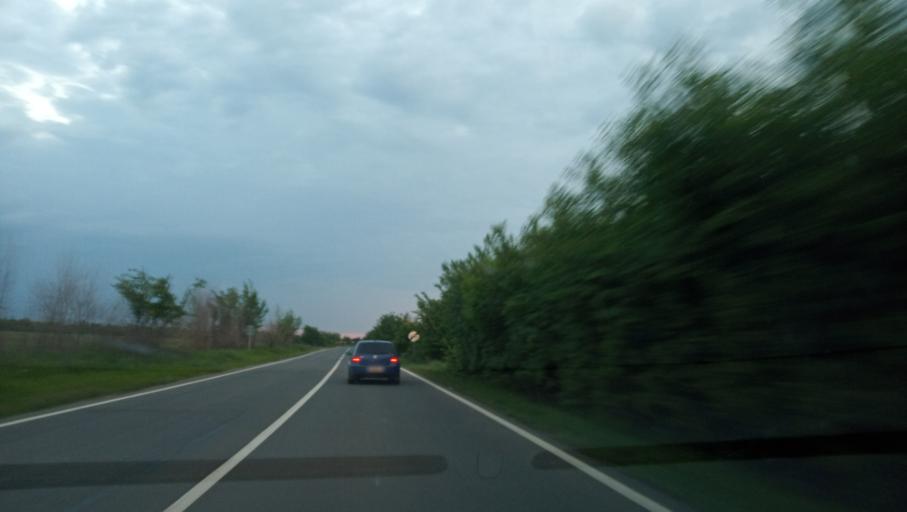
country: RO
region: Timis
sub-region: Comuna Padureni
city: Padureni
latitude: 45.6178
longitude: 21.1950
